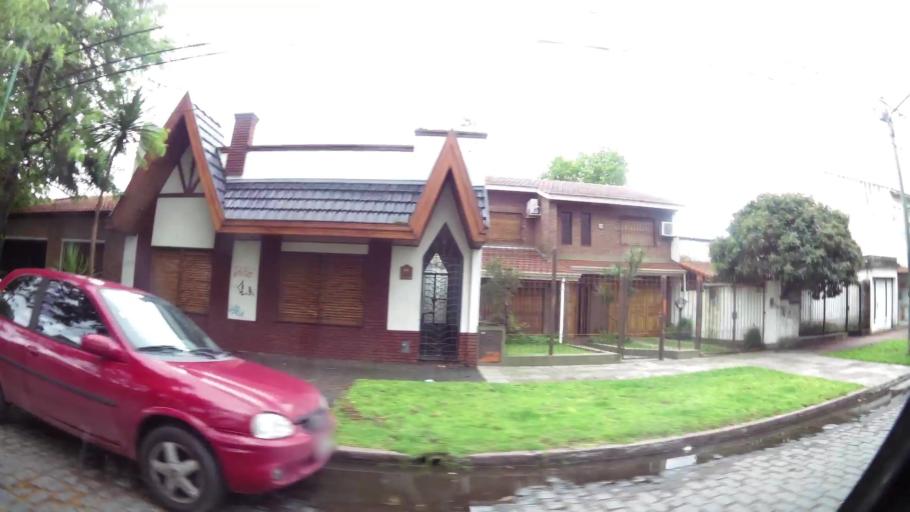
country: AR
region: Buenos Aires
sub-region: Partido de Lomas de Zamora
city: Lomas de Zamora
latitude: -34.7473
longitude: -58.3917
